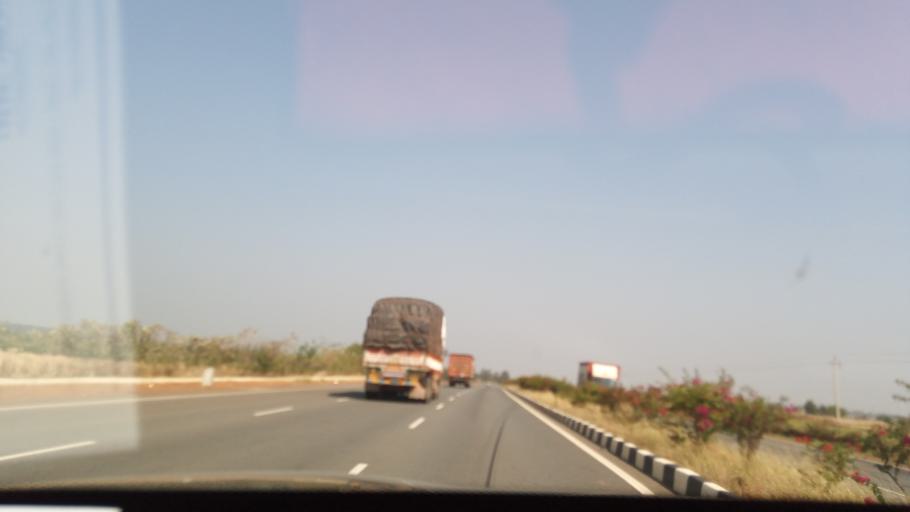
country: IN
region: Karnataka
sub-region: Haveri
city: Shiggaon
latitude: 15.0758
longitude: 75.1543
